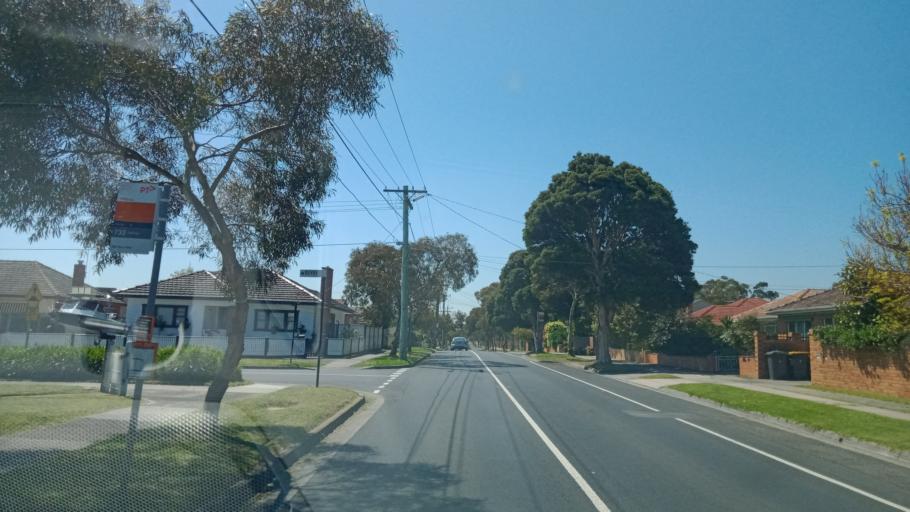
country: AU
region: Victoria
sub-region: Monash
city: Oakleigh South
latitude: -37.9180
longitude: 145.0881
